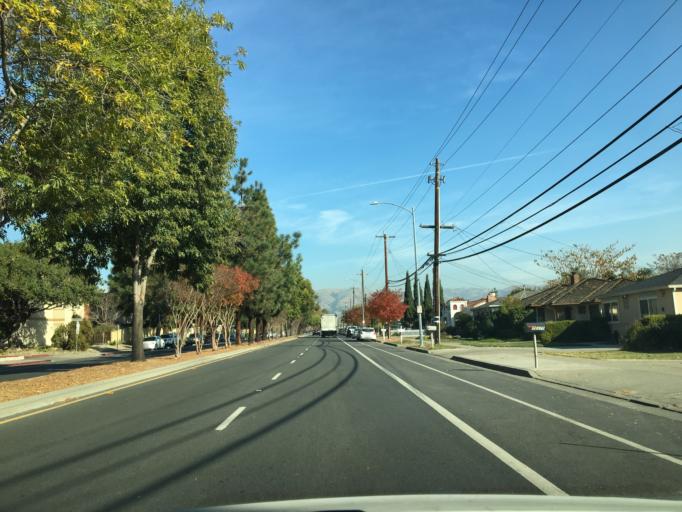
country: US
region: California
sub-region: Santa Clara County
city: San Jose
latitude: 37.3678
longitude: -121.8679
